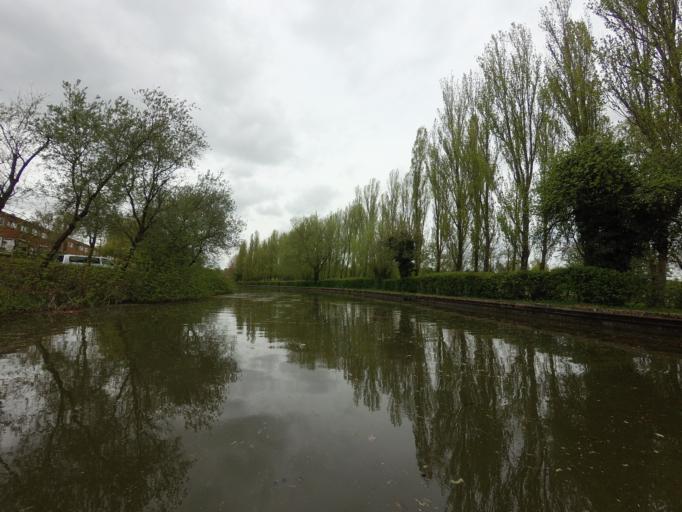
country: GB
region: England
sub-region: Milton Keynes
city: Milton Keynes
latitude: 52.0350
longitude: -0.7303
